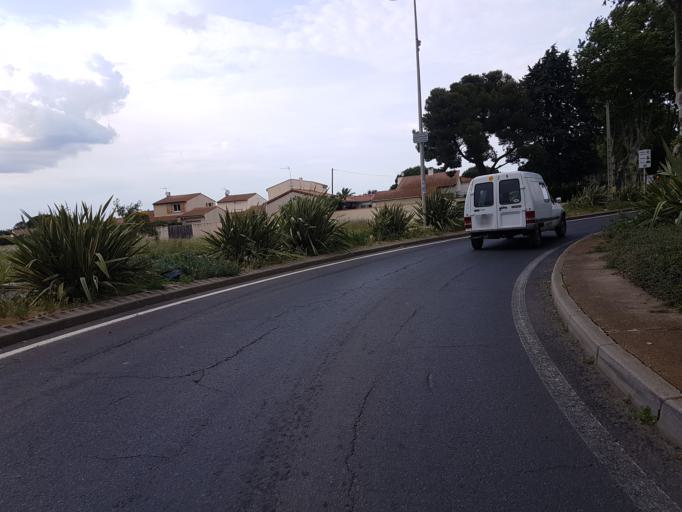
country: FR
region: Languedoc-Roussillon
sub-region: Departement de l'Herault
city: Cers
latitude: 43.3197
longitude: 3.3028
